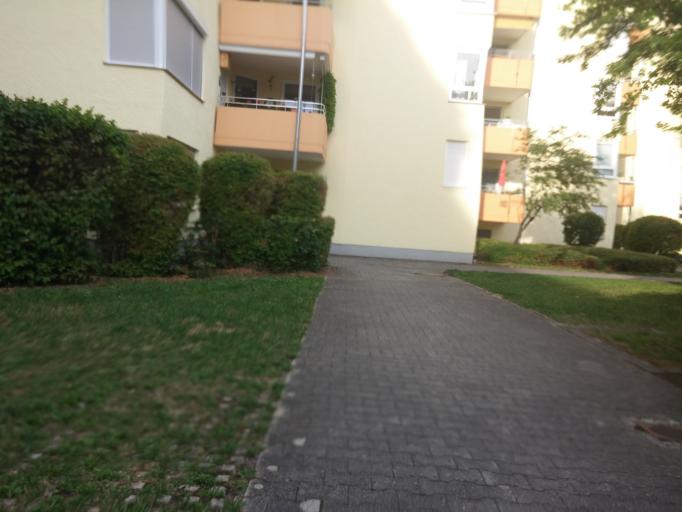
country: DE
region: Bavaria
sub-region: Upper Bavaria
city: Haar
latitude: 48.1062
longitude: 11.7198
